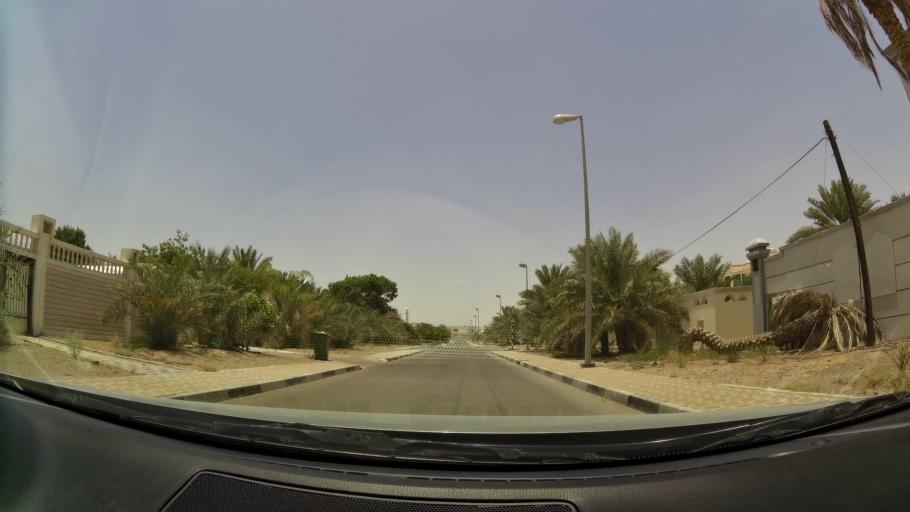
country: OM
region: Al Buraimi
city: Al Buraymi
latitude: 24.2683
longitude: 55.7244
